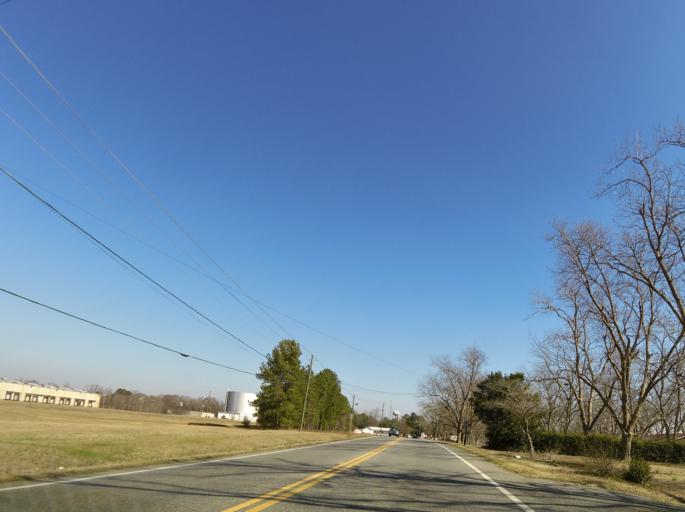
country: US
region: Georgia
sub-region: Bleckley County
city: Cochran
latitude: 32.3752
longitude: -83.3674
